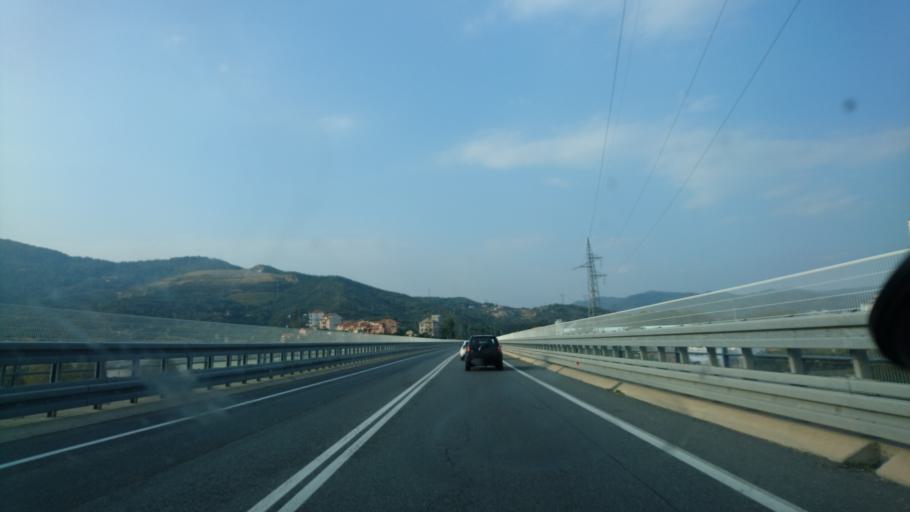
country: IT
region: Liguria
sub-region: Provincia di Savona
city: Vado Centro
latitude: 44.2632
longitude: 8.4270
